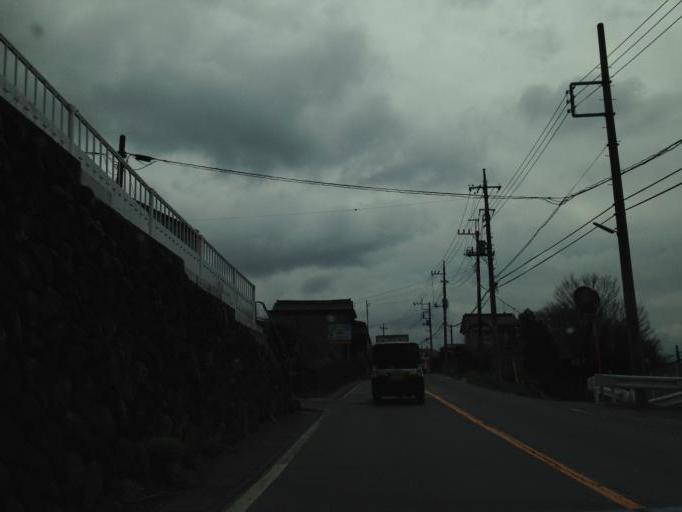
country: JP
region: Saitama
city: Chichibu
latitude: 36.0097
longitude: 139.0877
